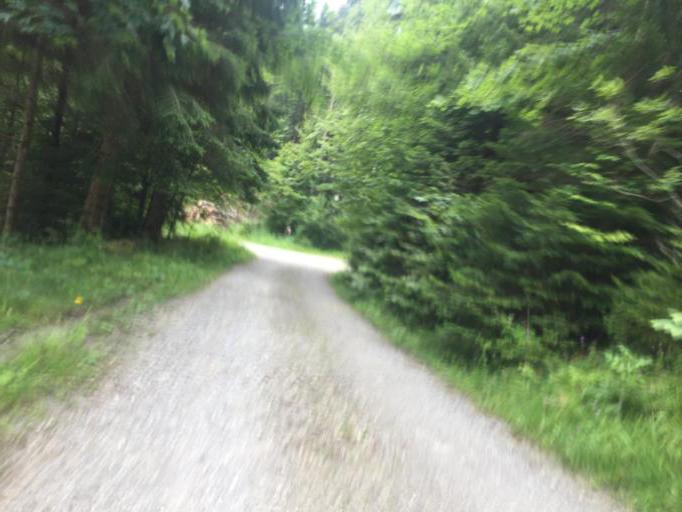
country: CH
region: Bern
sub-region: Thun District
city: Wattenwil
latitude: 46.7558
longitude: 7.4803
